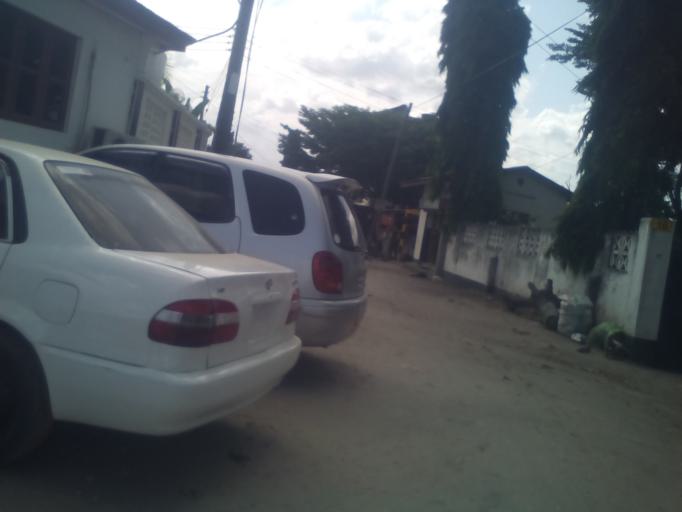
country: TZ
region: Dar es Salaam
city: Dar es Salaam
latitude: -6.8456
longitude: 39.2772
